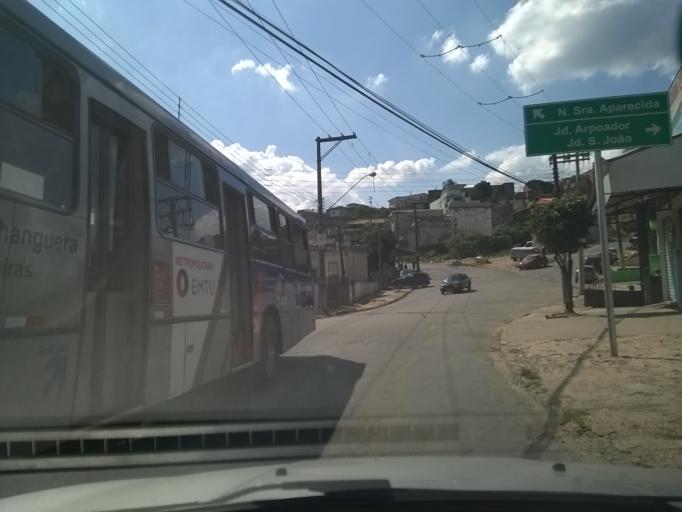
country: BR
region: Sao Paulo
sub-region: Francisco Morato
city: Francisco Morato
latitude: -23.2645
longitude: -46.7418
